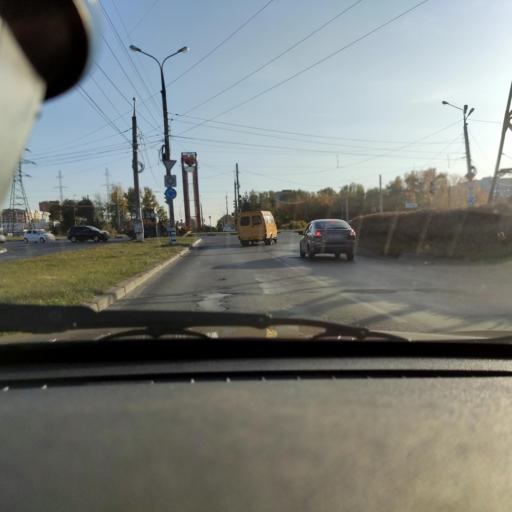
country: RU
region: Samara
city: Tol'yatti
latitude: 53.5517
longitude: 49.3181
